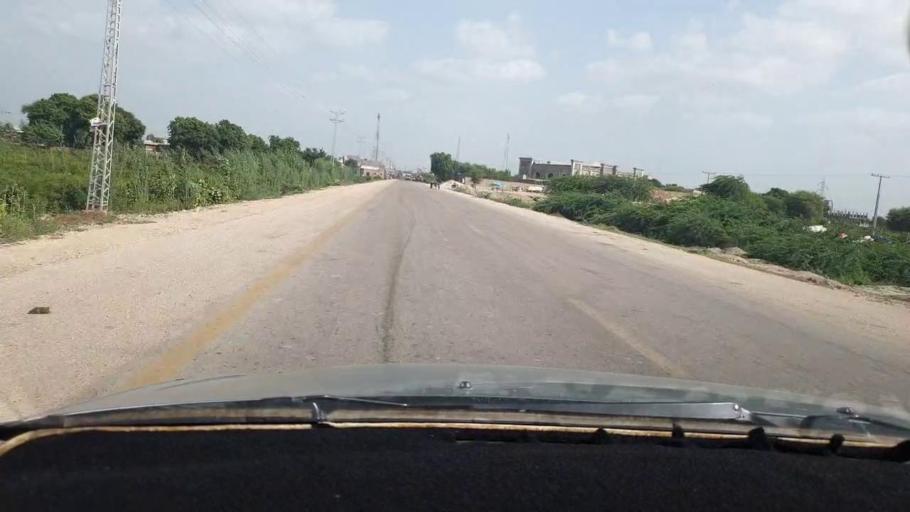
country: PK
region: Sindh
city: Naukot
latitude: 24.8598
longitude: 69.3940
